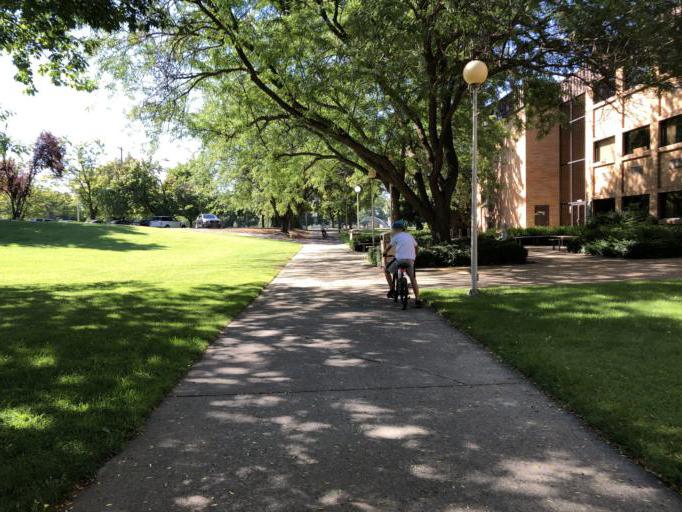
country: US
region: Washington
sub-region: Walla Walla County
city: College Place
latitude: 46.0467
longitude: -118.3929
